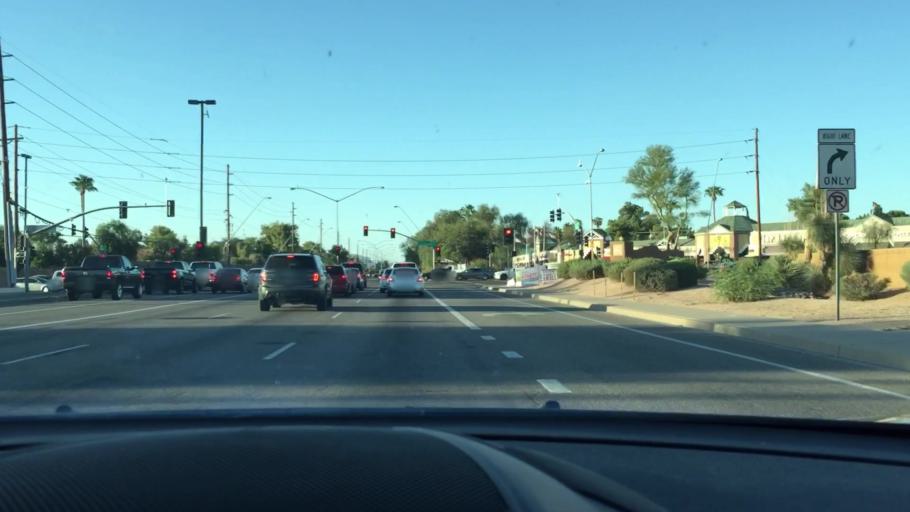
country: US
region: Arizona
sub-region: Maricopa County
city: Gilbert
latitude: 33.3931
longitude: -111.6847
